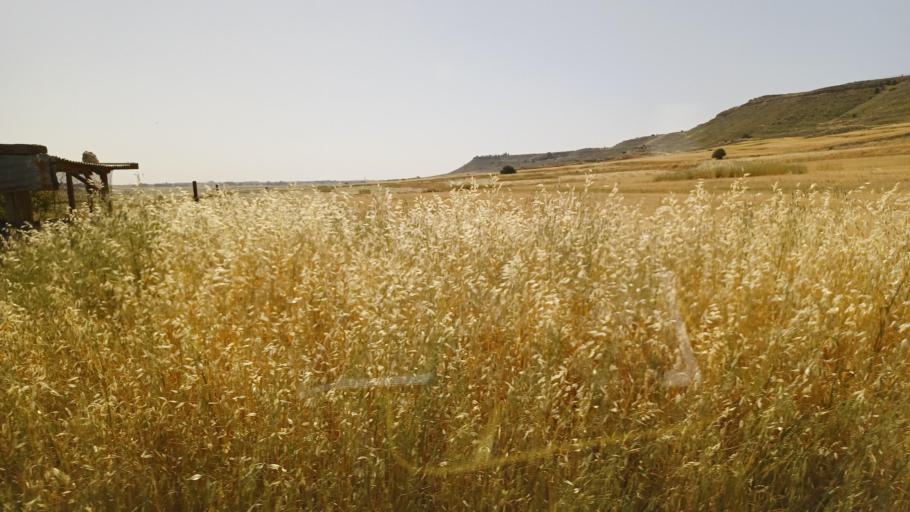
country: CY
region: Lefkosia
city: Mammari
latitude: 35.1741
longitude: 33.2186
